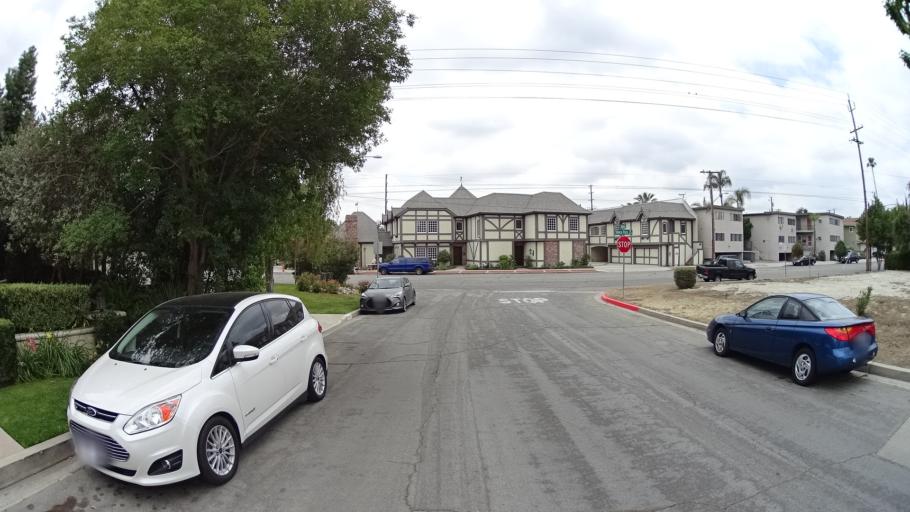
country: US
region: California
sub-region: Los Angeles County
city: Universal City
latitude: 34.1595
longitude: -118.3506
